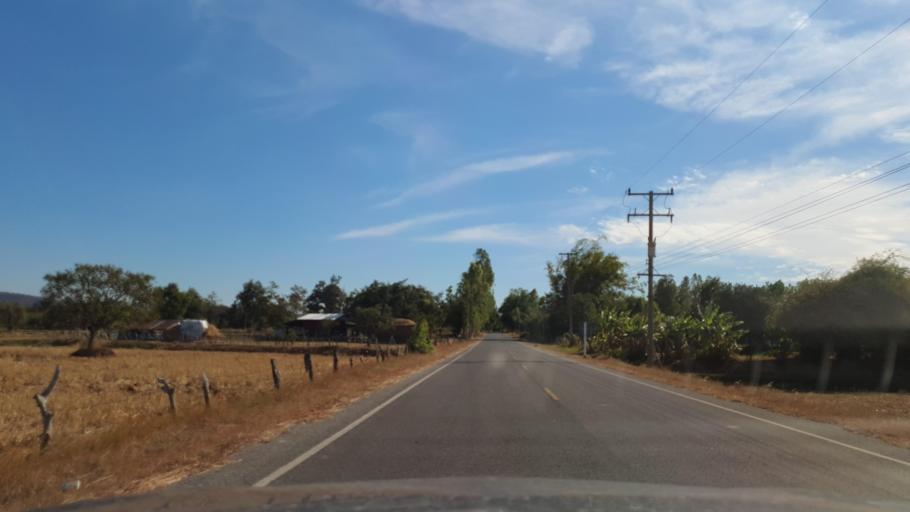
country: TH
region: Kalasin
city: Khao Wong
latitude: 16.6206
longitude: 104.1355
